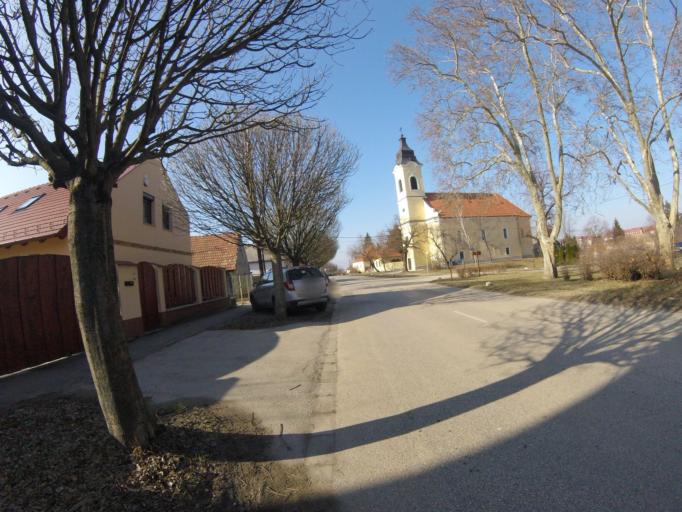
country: HU
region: Komarom-Esztergom
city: Oroszlany
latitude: 47.4879
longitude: 18.3229
